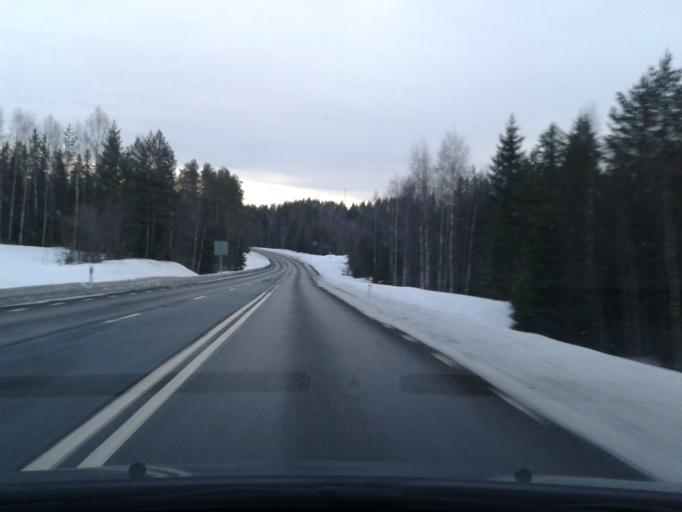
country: SE
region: Vaesternorrland
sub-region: Kramfors Kommun
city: Bollstabruk
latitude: 63.1027
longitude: 17.5109
